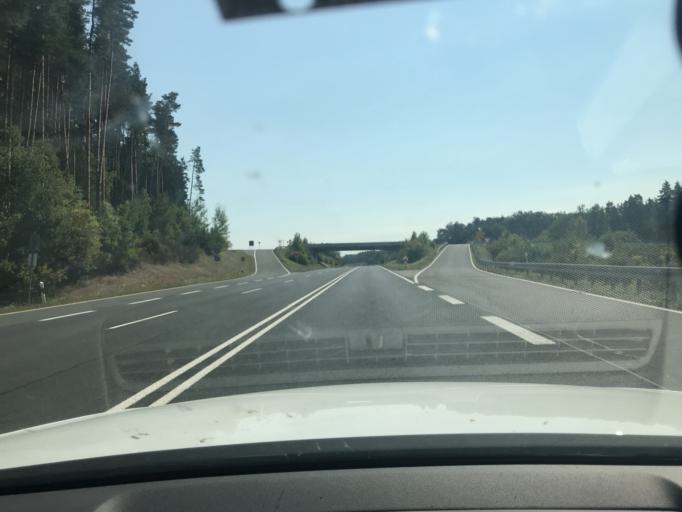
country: DE
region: Bavaria
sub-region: Upper Palatinate
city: Poppenricht
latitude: 49.4653
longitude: 11.7807
